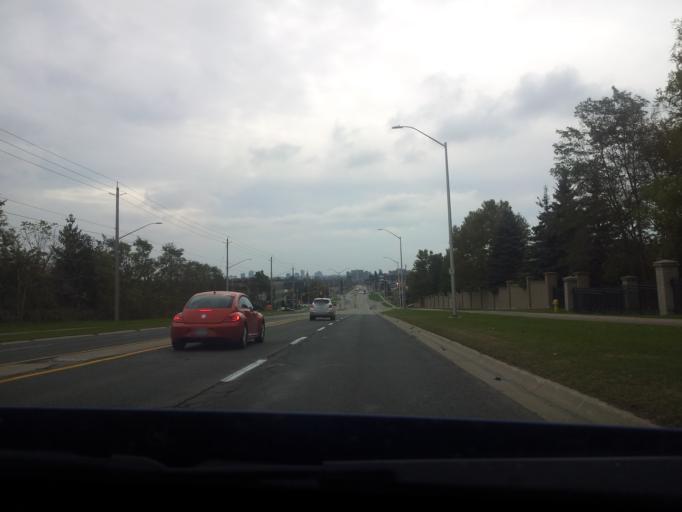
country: CA
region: Ontario
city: London
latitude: 43.0313
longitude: -81.2852
